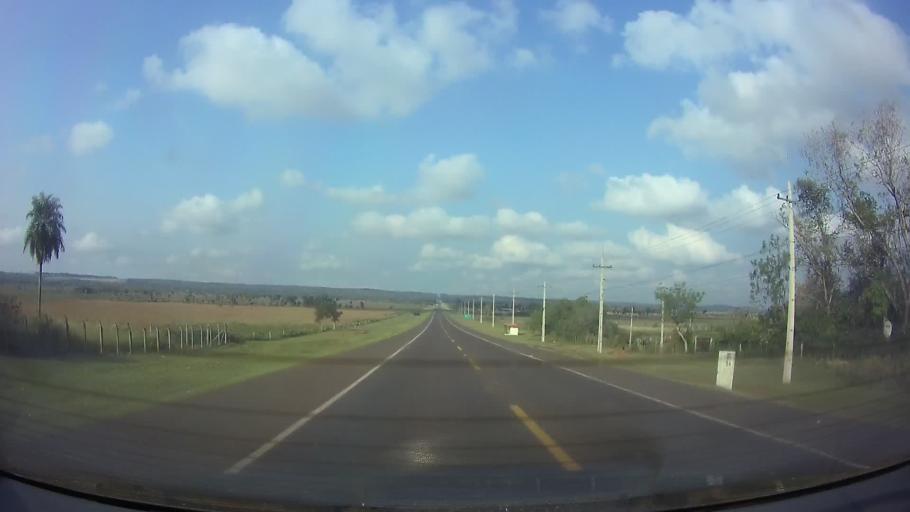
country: PY
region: Cordillera
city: Arroyos y Esteros
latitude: -25.0650
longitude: -57.2042
